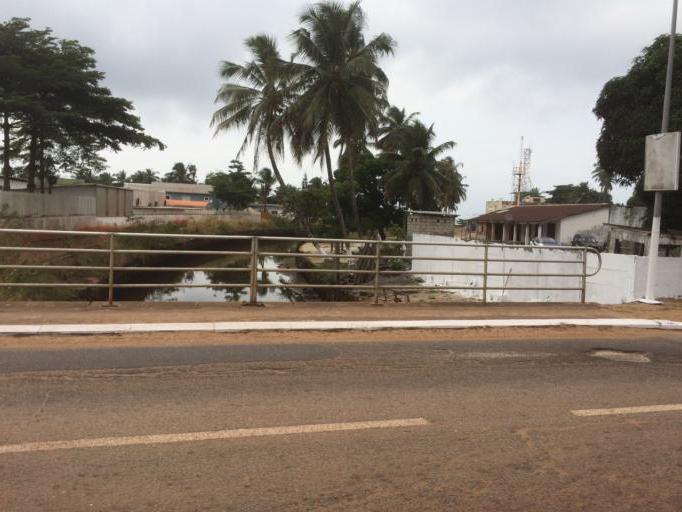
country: GA
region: Ogooue-Maritime
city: Port-Gentil
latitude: -0.7082
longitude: 8.7802
